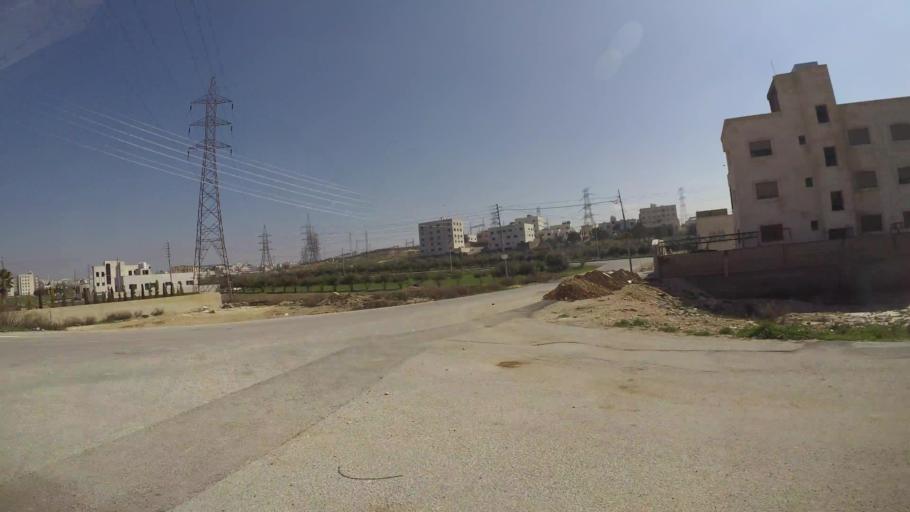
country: JO
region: Amman
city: Al Bunayyat ash Shamaliyah
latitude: 31.8915
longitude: 35.9018
